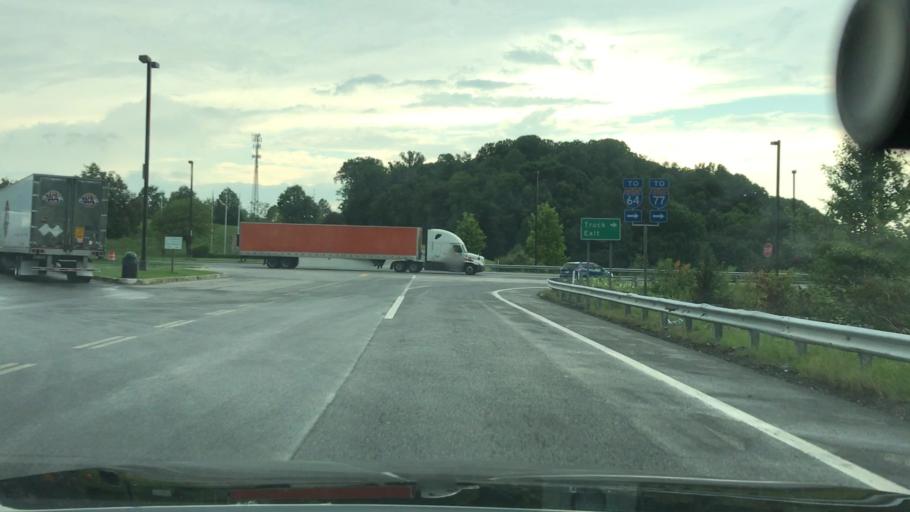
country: US
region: West Virginia
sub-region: Raleigh County
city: Mabscott
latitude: 37.8028
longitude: -81.2145
